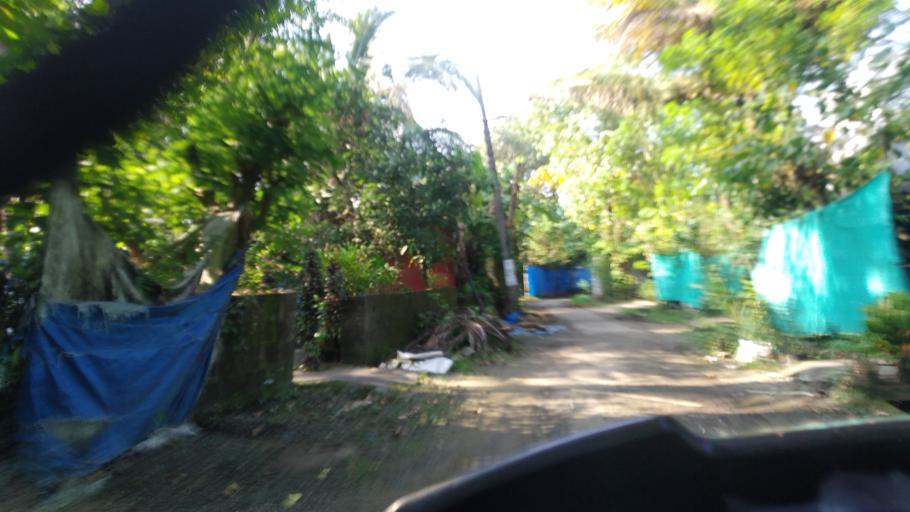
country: IN
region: Kerala
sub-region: Ernakulam
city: Cochin
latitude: 9.9911
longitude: 76.2243
